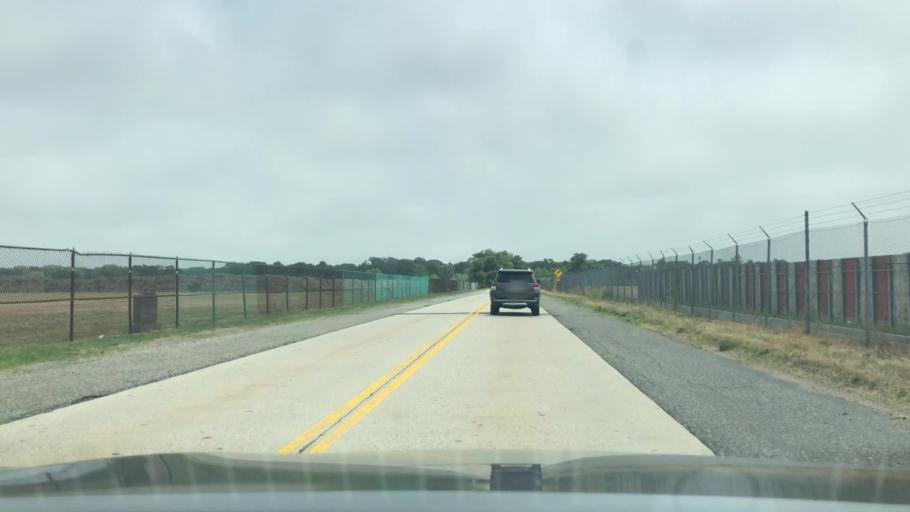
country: US
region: New York
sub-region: Suffolk County
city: East Farmingdale
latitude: 40.7237
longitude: -73.4031
